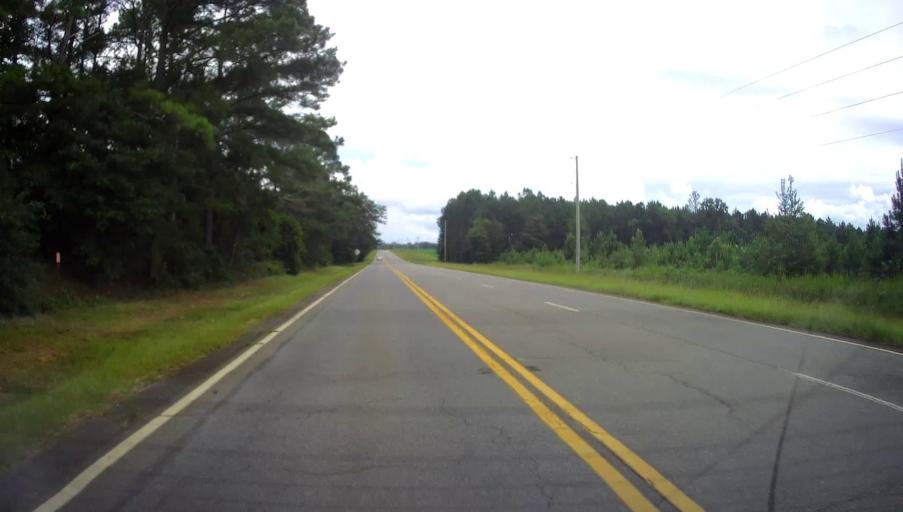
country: US
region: Georgia
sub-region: Schley County
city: Ellaville
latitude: 32.2554
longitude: -84.3541
